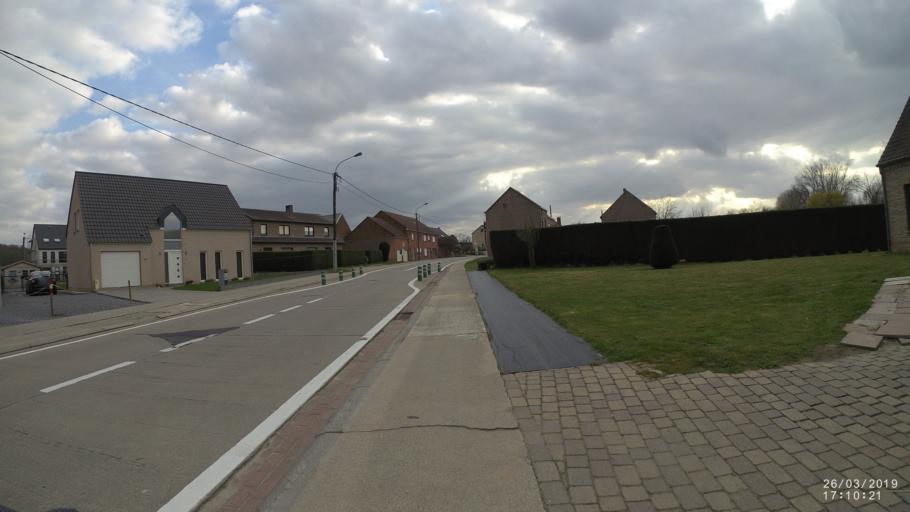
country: BE
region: Flanders
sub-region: Provincie Vlaams-Brabant
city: Huldenberg
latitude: 50.8374
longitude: 4.5741
